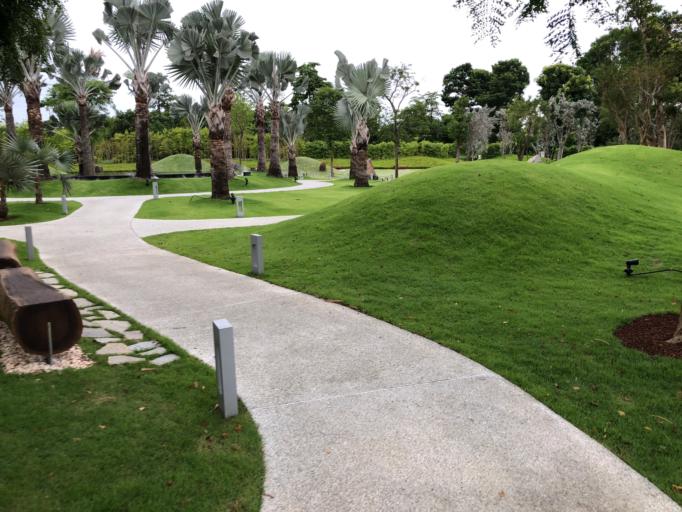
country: SG
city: Singapore
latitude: 1.2787
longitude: 103.8610
